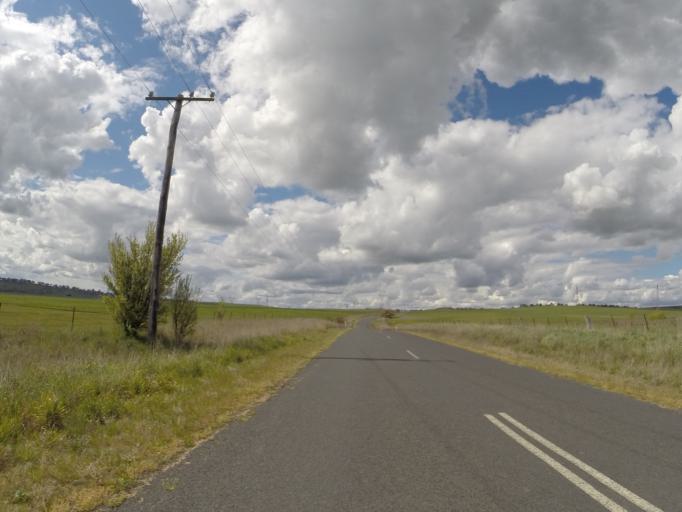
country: AU
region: New South Wales
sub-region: Yass Valley
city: Yass
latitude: -34.8784
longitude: 148.8990
